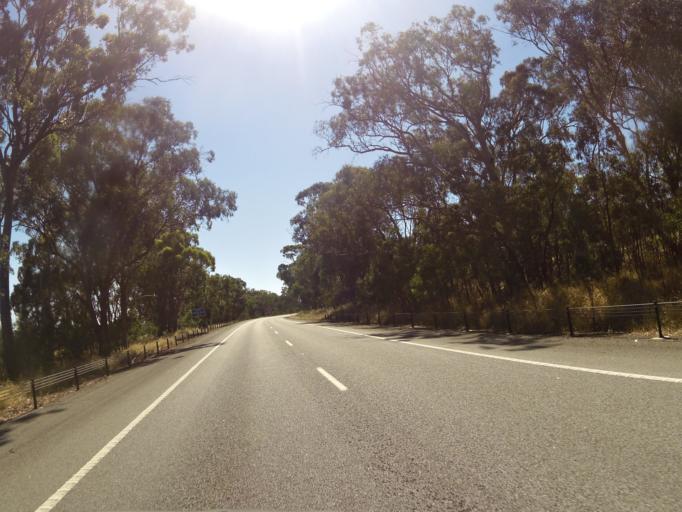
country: AU
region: Victoria
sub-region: Greater Shepparton
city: Shepparton
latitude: -36.7718
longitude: 145.5199
